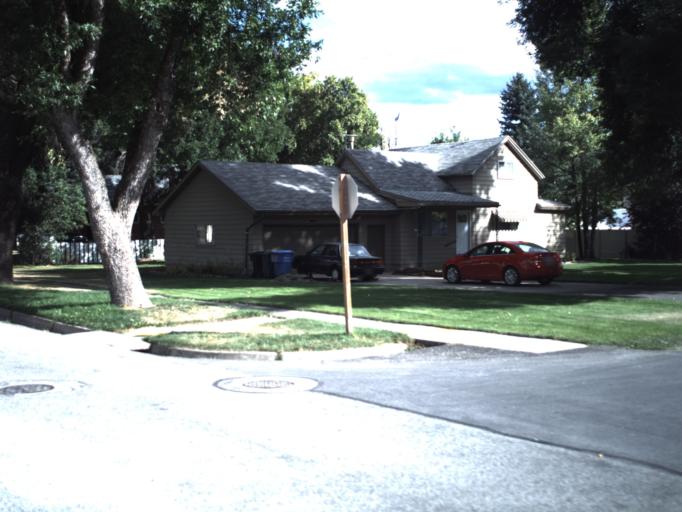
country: US
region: Utah
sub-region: Cache County
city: Wellsville
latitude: 41.6386
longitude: -111.9289
